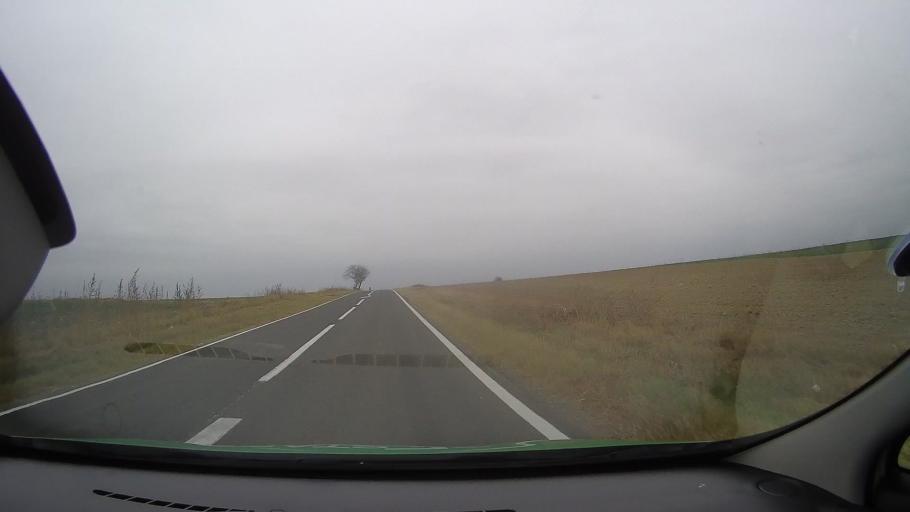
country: RO
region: Constanta
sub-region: Comuna Ghindaresti
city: Ghindaresti
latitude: 44.7038
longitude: 28.0412
